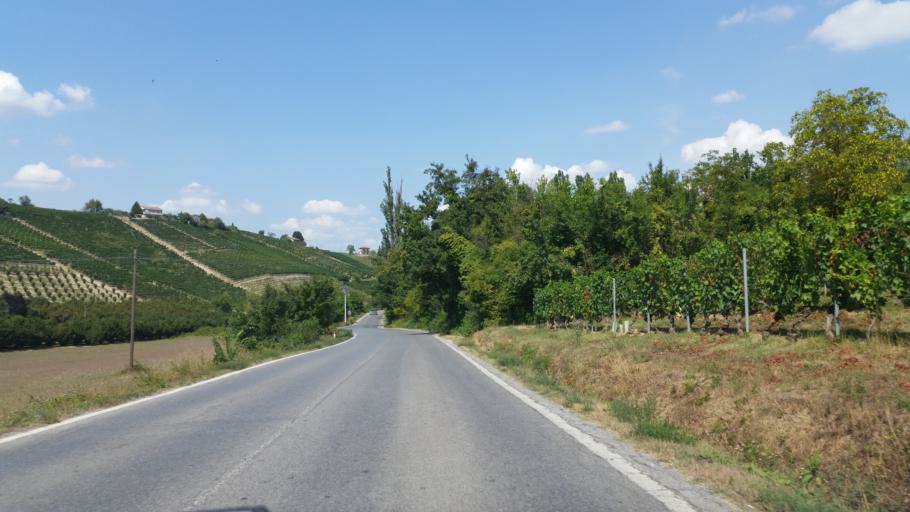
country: IT
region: Piedmont
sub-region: Provincia di Cuneo
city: Alba
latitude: 44.6949
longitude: 8.0535
